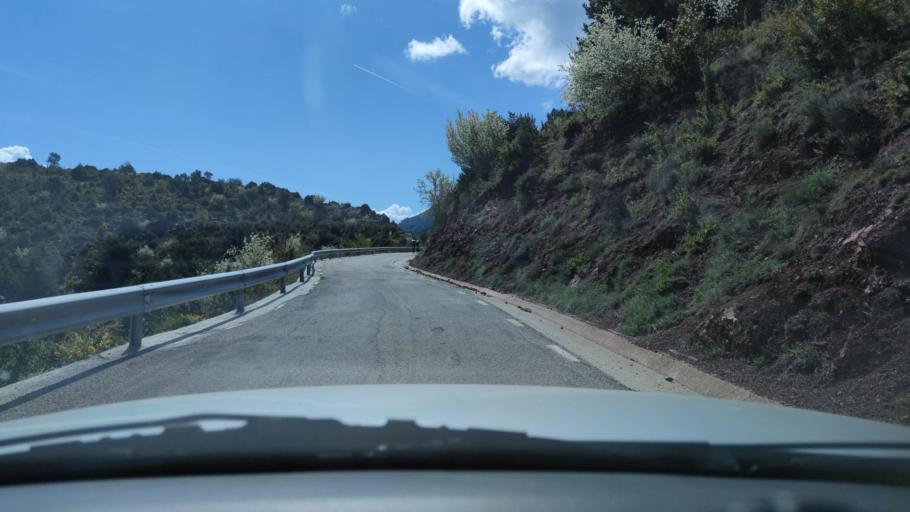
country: ES
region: Catalonia
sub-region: Provincia de Lleida
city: Coll de Nargo
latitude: 42.3050
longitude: 1.2826
